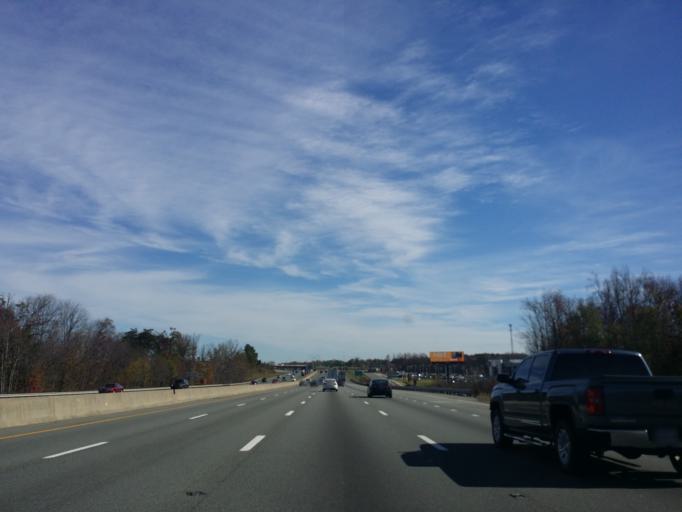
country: US
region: North Carolina
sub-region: Alamance County
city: Elon
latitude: 36.0641
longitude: -79.5274
